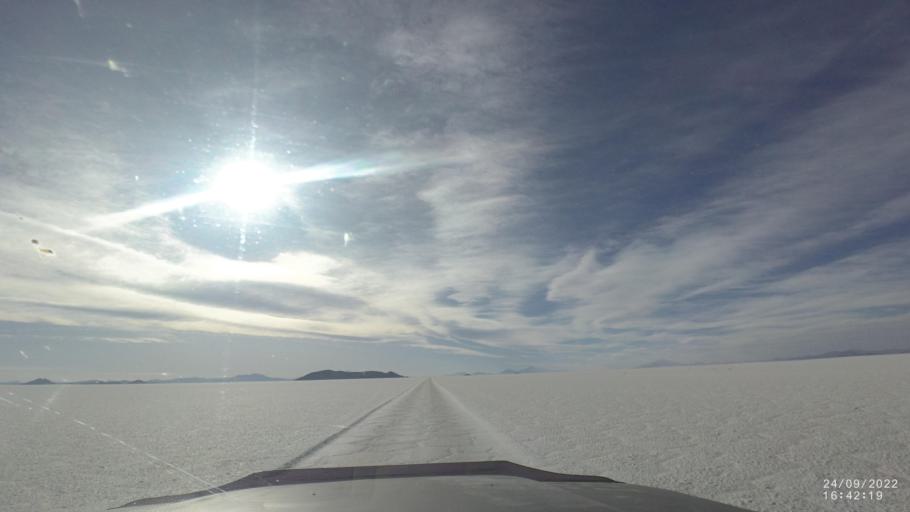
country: BO
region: Potosi
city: Colchani
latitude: -20.1762
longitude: -67.7300
